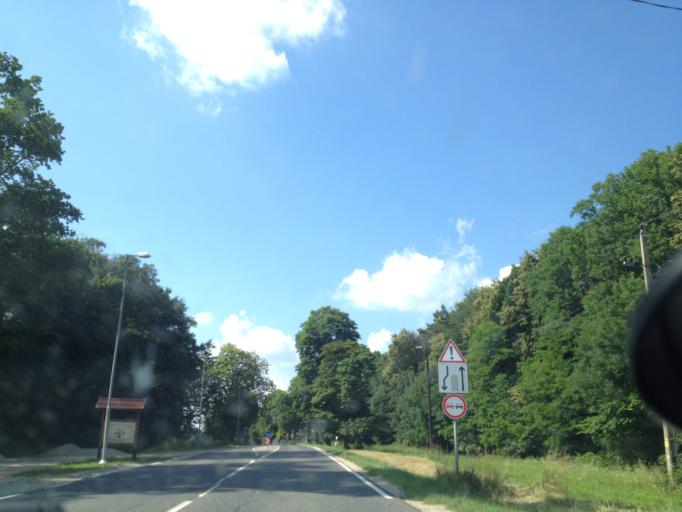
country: HU
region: Veszprem
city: Urkut
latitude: 47.2073
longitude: 17.6242
